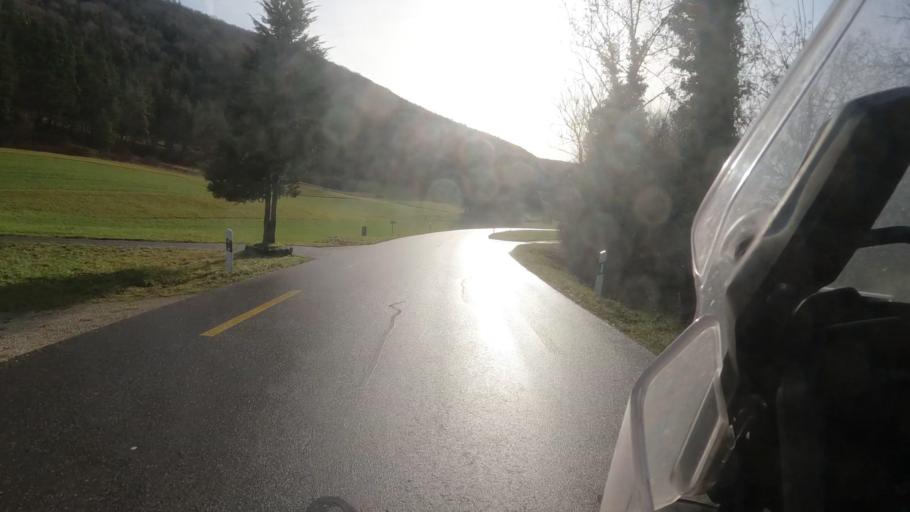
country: CH
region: Schaffhausen
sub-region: Bezirk Reiat
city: Stetten
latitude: 47.7795
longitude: 8.6185
